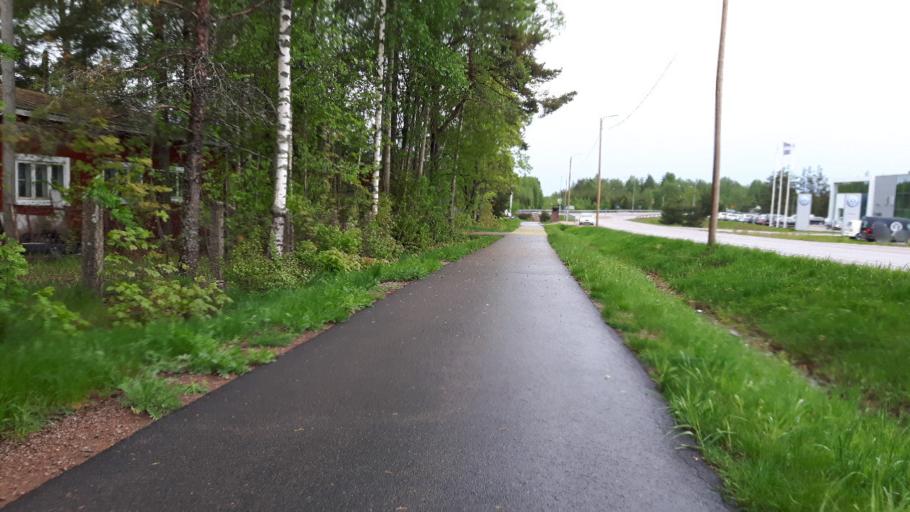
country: FI
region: Kymenlaakso
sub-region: Kotka-Hamina
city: Karhula
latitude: 60.5403
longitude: 26.9712
